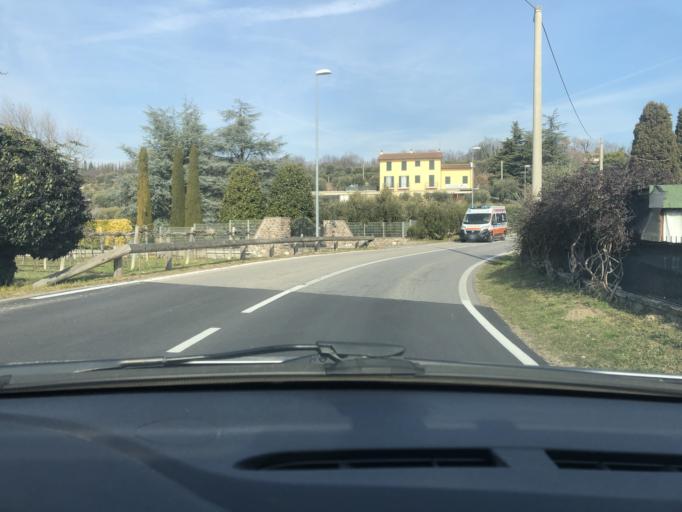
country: IT
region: Veneto
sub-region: Provincia di Verona
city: Garda
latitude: 45.5650
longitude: 10.7296
